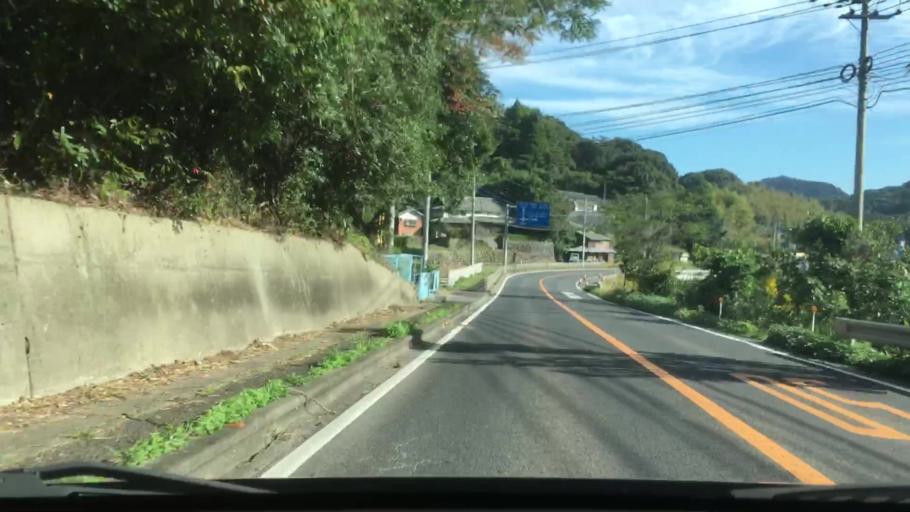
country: JP
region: Nagasaki
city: Sasebo
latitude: 33.1017
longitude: 129.7647
